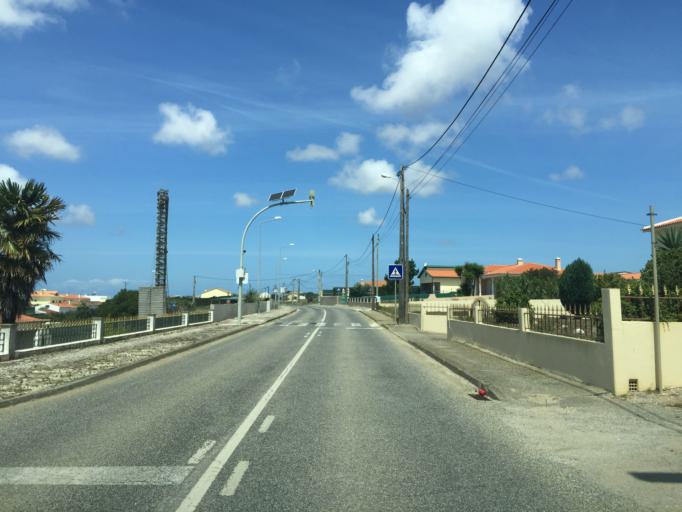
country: PT
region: Lisbon
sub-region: Lourinha
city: Lourinha
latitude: 39.2839
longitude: -9.3026
